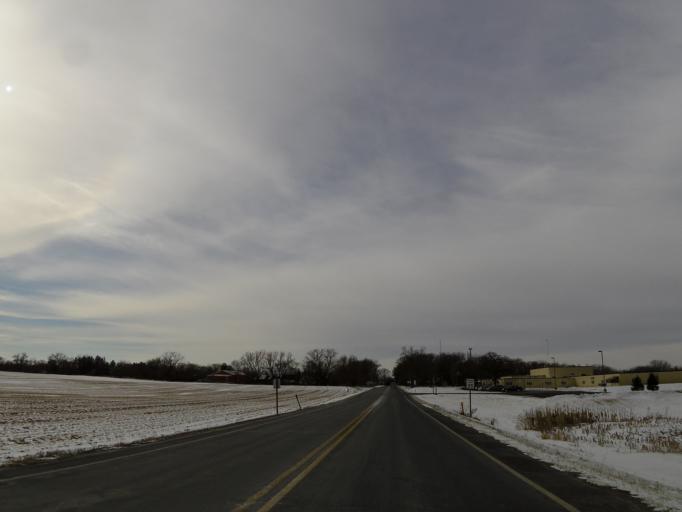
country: US
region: Minnesota
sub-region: Washington County
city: Stillwater
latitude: 45.0607
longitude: -92.7835
